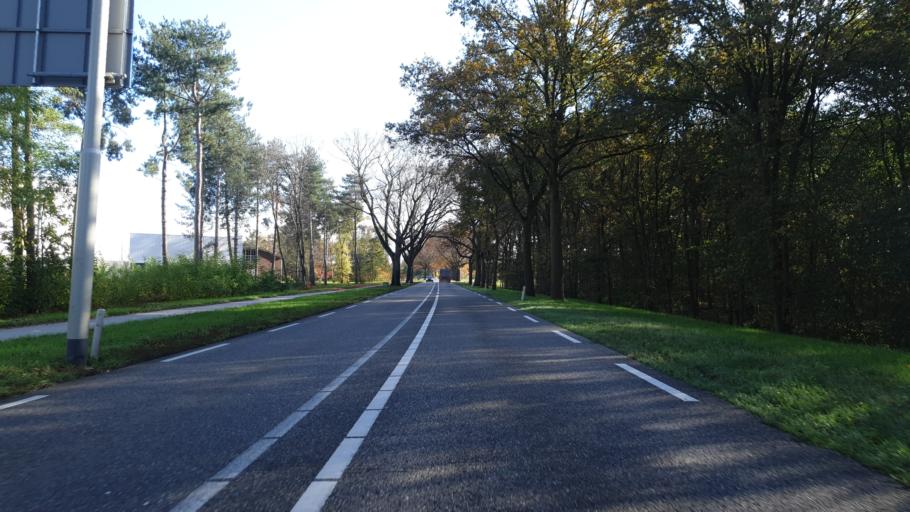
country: NL
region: North Brabant
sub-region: Gemeente Boxmeer
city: Overloon
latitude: 51.6088
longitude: 6.0384
